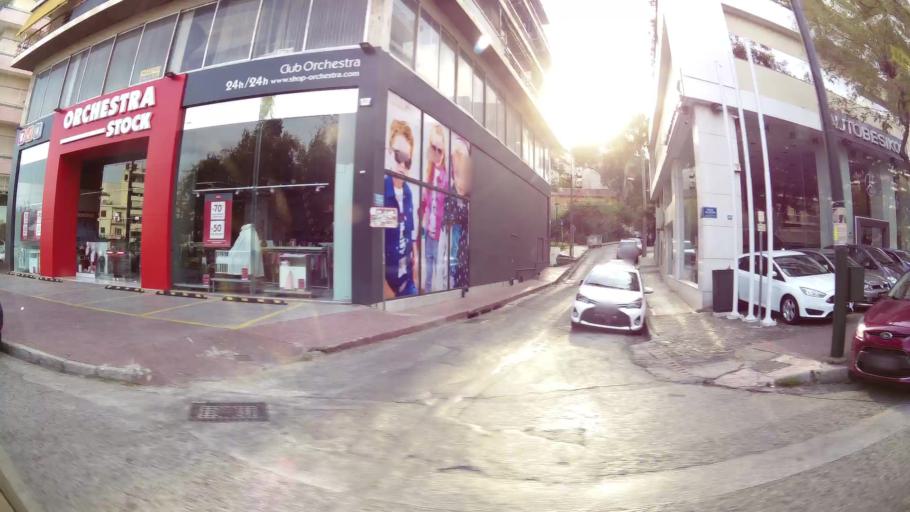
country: GR
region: Attica
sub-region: Nomarchia Athinas
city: Nea Chalkidona
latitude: 38.0254
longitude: 23.7312
